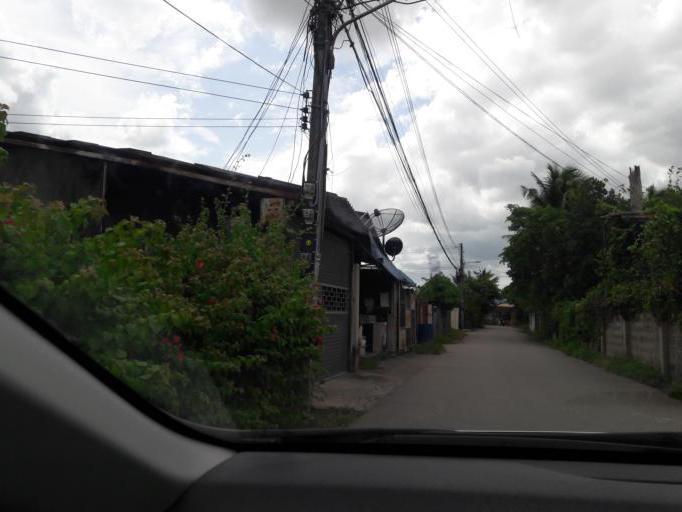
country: TH
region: Ratchaburi
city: Ratchaburi
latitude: 13.5345
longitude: 99.7951
